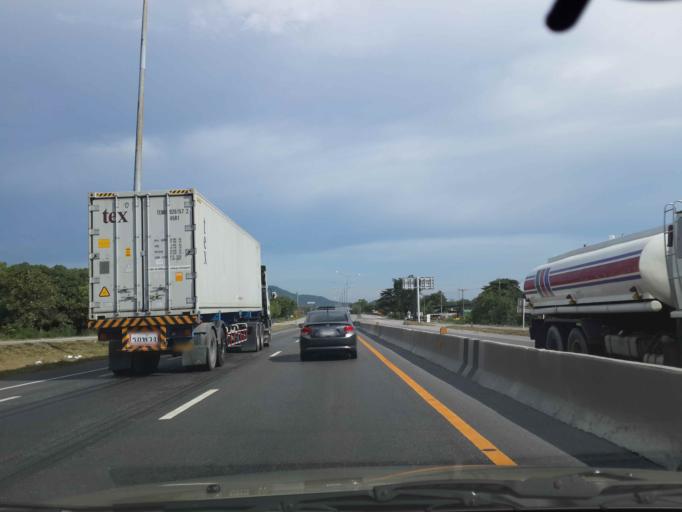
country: TH
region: Chon Buri
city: Chon Buri
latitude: 13.3290
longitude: 100.9897
